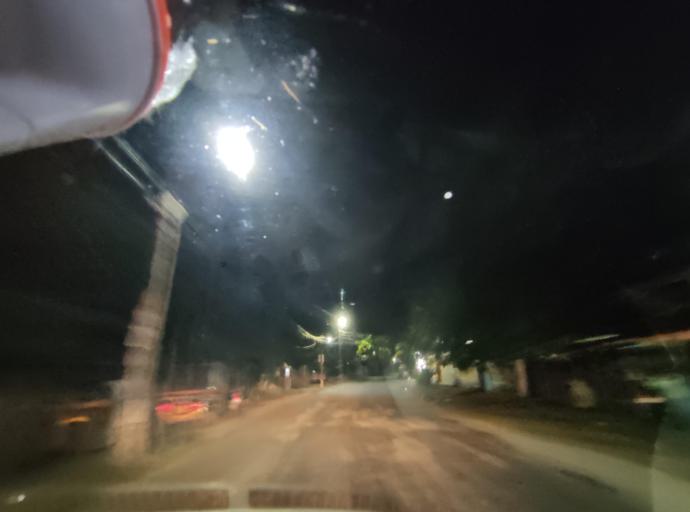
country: IN
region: Kerala
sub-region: Thiruvananthapuram
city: Thiruvananthapuram
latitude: 8.4682
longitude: 76.9233
